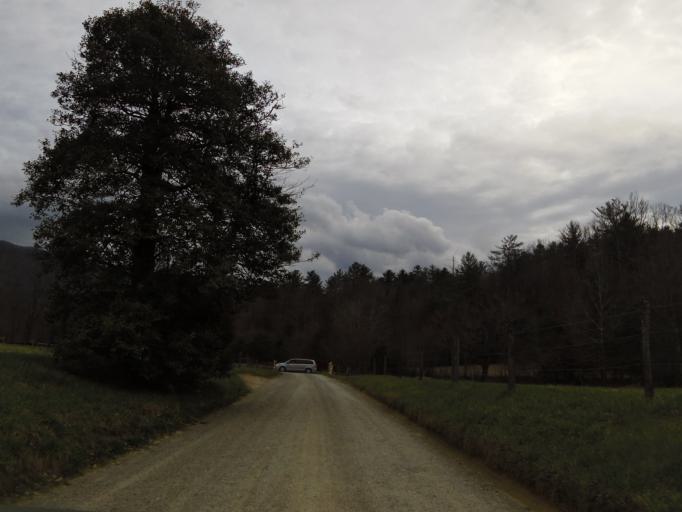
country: US
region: Tennessee
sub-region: Blount County
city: Wildwood
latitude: 35.5890
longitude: -83.8226
